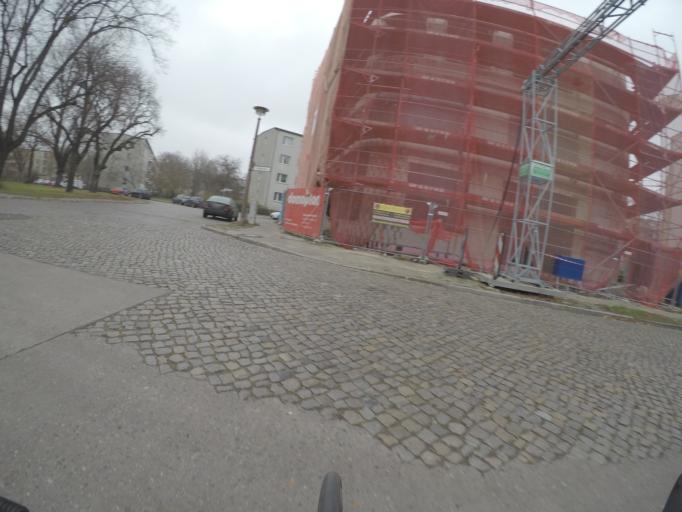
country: DE
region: Berlin
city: Oberschoneweide
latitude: 52.4592
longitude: 13.5335
